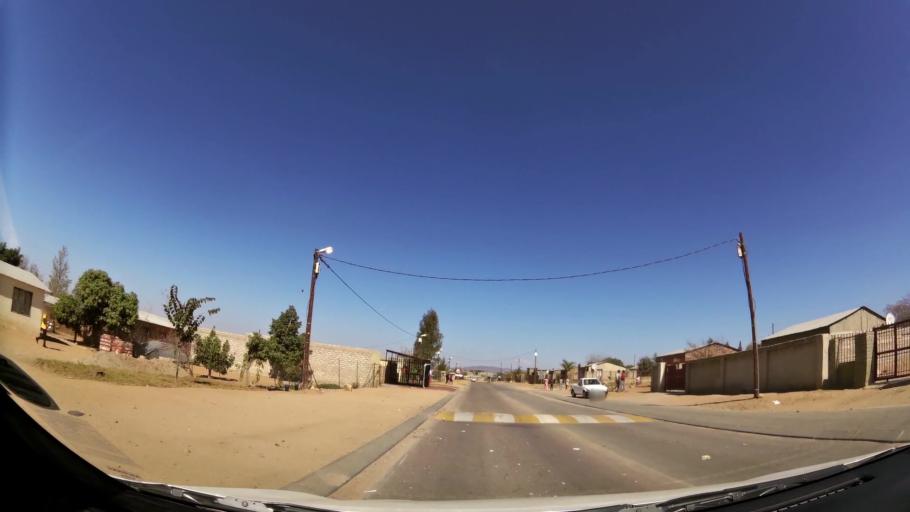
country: ZA
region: Limpopo
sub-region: Capricorn District Municipality
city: Polokwane
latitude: -23.8824
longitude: 29.4097
